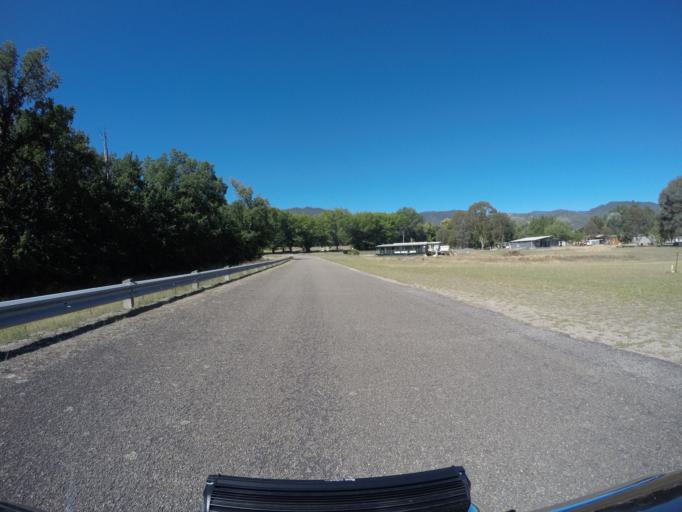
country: AU
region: New South Wales
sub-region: Snowy River
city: Jindabyne
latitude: -36.2195
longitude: 148.1187
